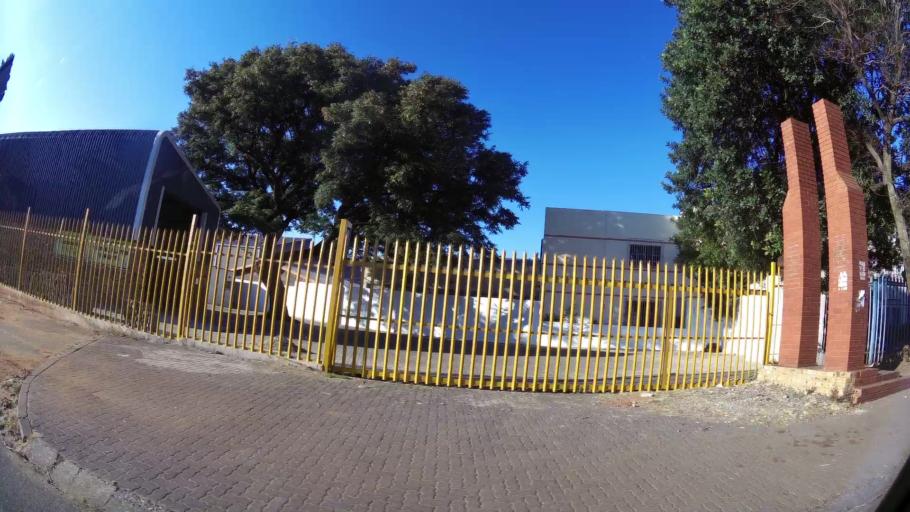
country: ZA
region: Gauteng
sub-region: City of Johannesburg Metropolitan Municipality
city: Johannesburg
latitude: -26.2076
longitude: 28.0818
